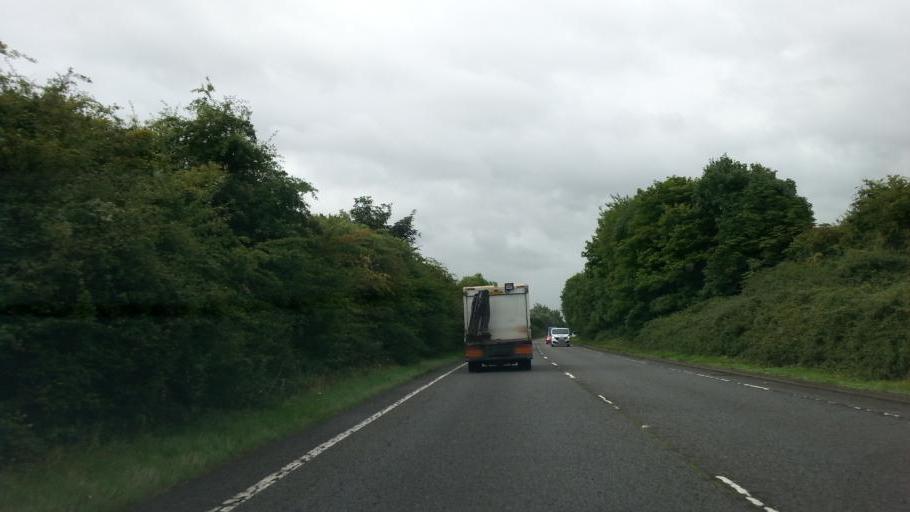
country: GB
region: England
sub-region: Northamptonshire
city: Oundle
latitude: 52.4730
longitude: -0.4570
